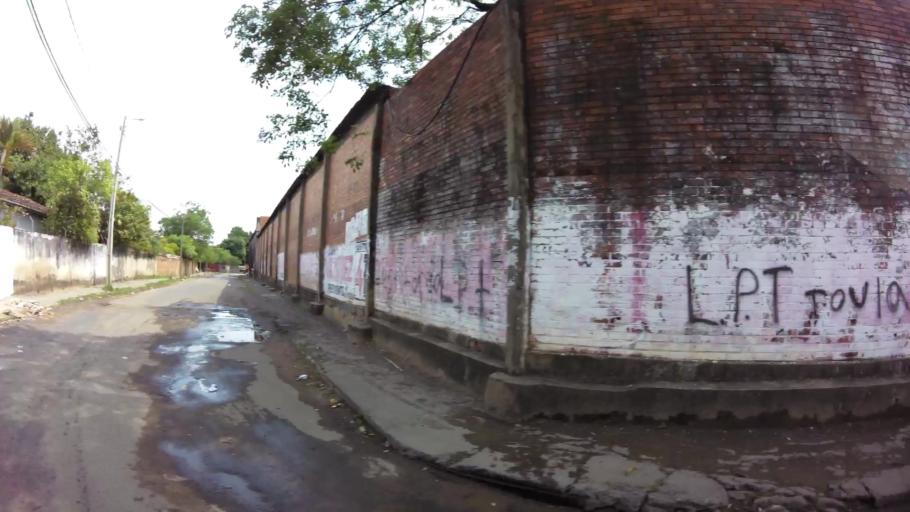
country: PY
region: Asuncion
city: Asuncion
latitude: -25.2630
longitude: -57.5851
